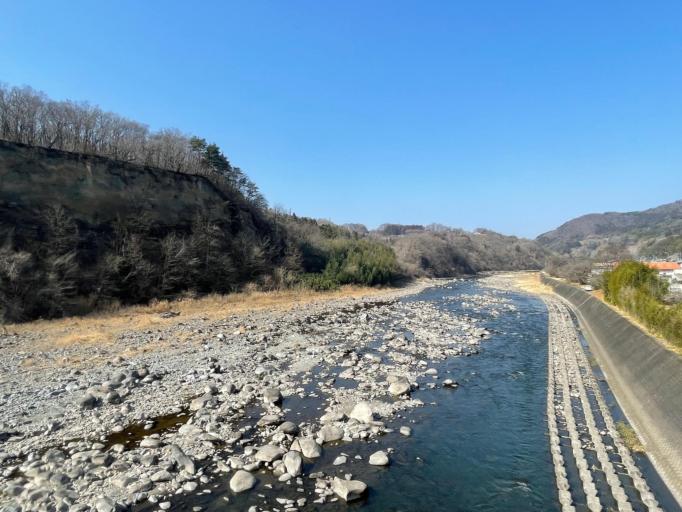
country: JP
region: Gunma
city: Shibukawa
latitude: 36.5464
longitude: 138.9557
